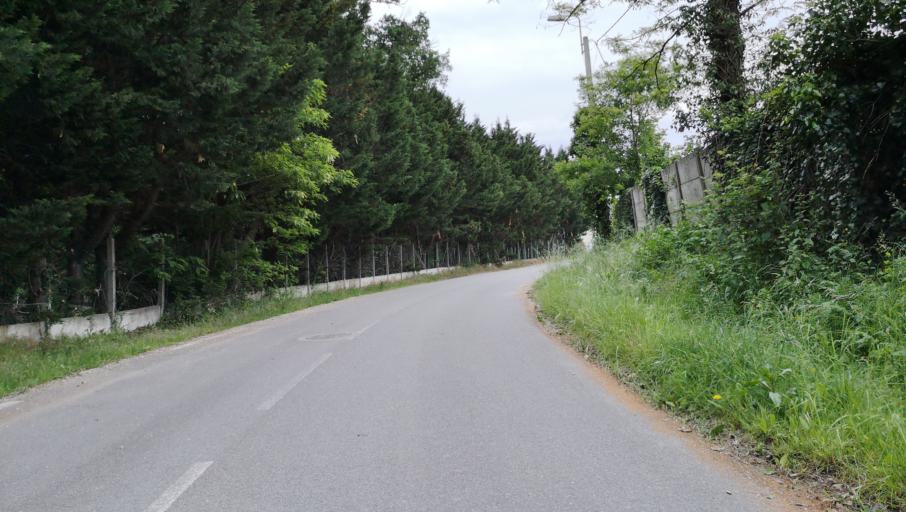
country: FR
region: Centre
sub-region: Departement du Loiret
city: Fleury-les-Aubrais
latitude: 47.9481
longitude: 1.9114
